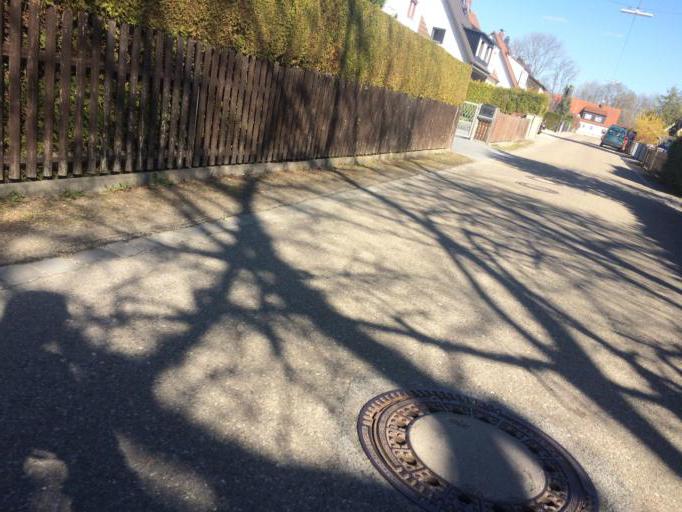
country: DE
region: Bavaria
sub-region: Swabia
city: Augsburg
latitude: 48.4029
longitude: 10.9148
